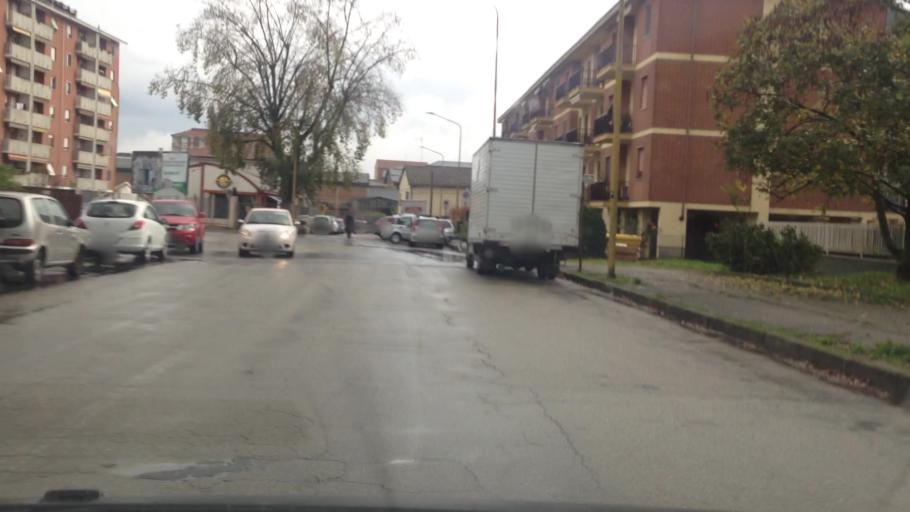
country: IT
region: Piedmont
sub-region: Provincia di Asti
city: Asti
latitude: 44.9077
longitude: 8.2201
